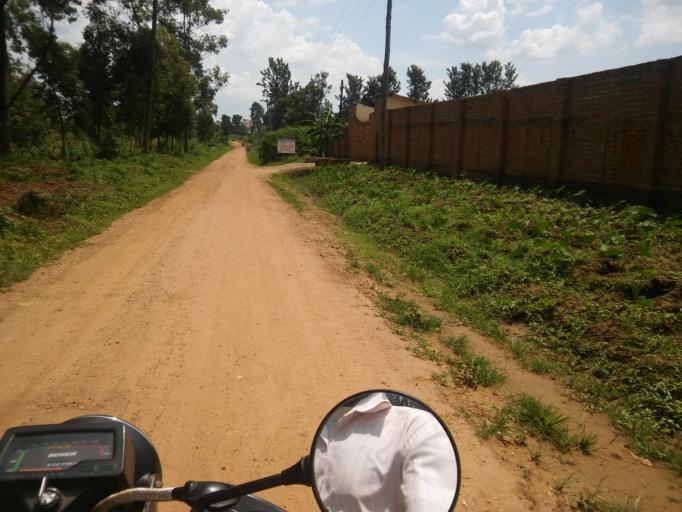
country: UG
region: Eastern Region
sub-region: Mbale District
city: Mbale
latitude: 1.0753
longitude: 34.1566
